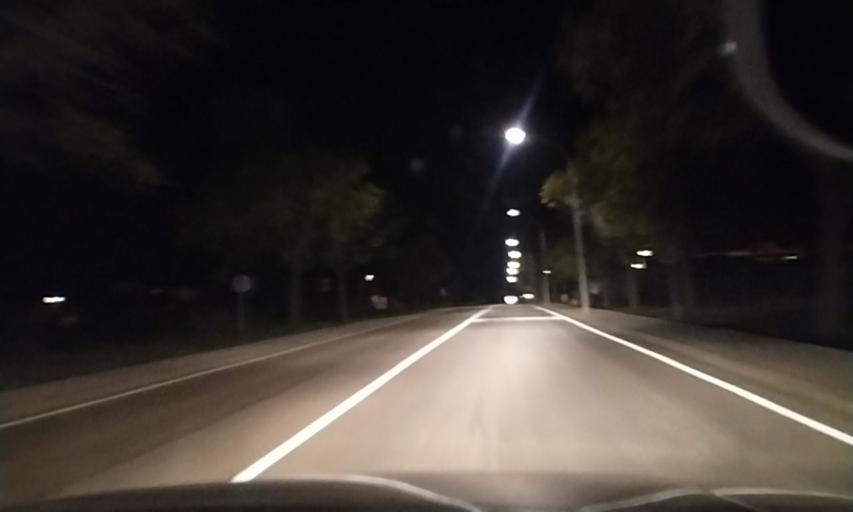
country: ES
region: Castille and Leon
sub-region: Provincia de Zamora
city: Benavente
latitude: 42.0100
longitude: -5.6873
